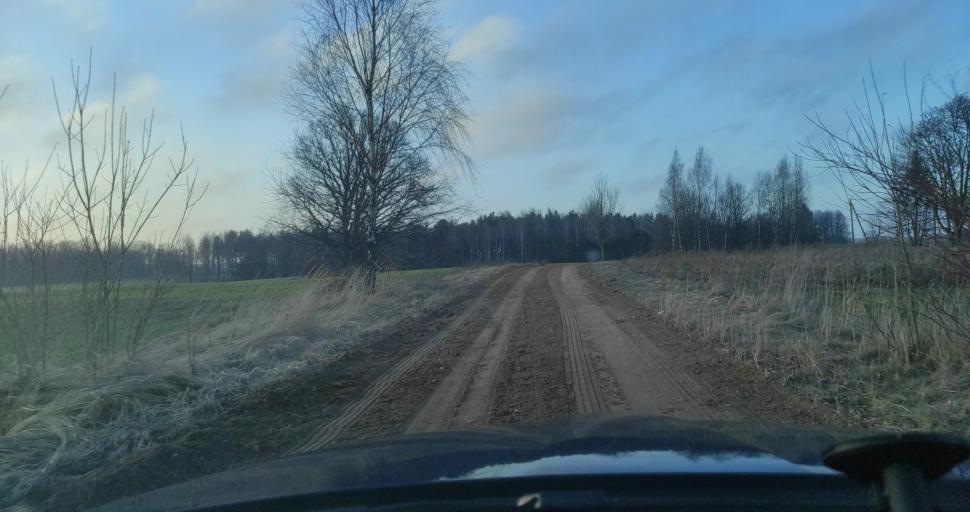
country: LV
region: Aizpute
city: Aizpute
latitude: 56.8015
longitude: 21.8043
